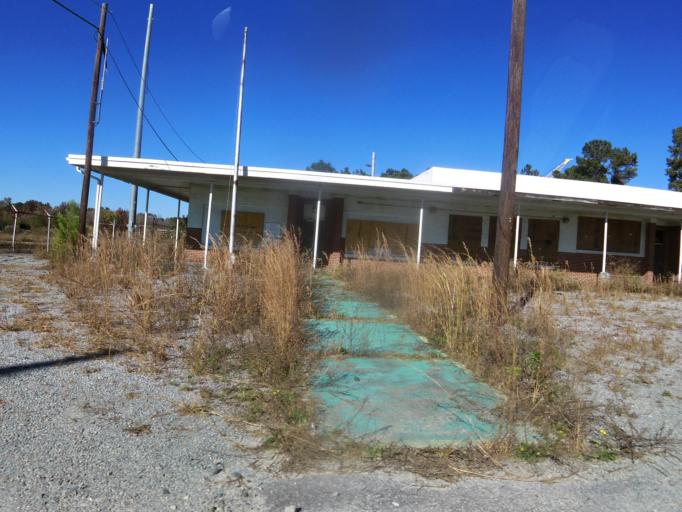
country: US
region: Georgia
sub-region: Chatham County
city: Garden City
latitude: 32.0706
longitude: -81.1450
